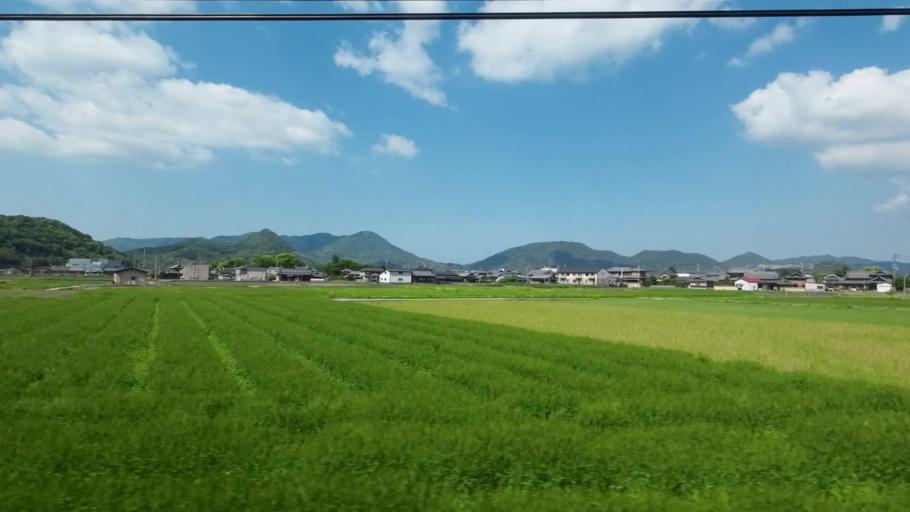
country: JP
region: Kagawa
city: Tadotsu
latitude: 34.2032
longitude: 133.7116
